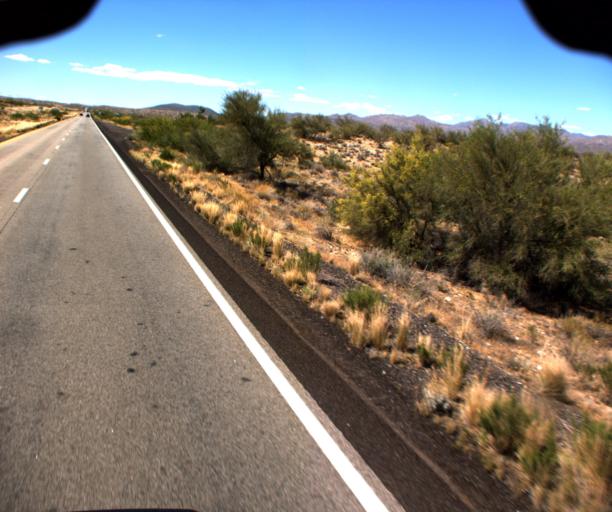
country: US
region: Arizona
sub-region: Mohave County
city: Kingman
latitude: 34.8742
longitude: -113.6457
